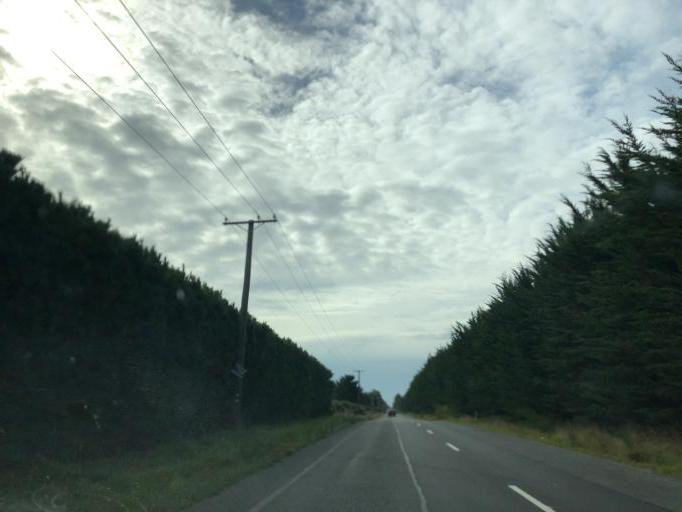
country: NZ
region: Canterbury
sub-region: Selwyn District
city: Rolleston
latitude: -43.6181
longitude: 172.4014
